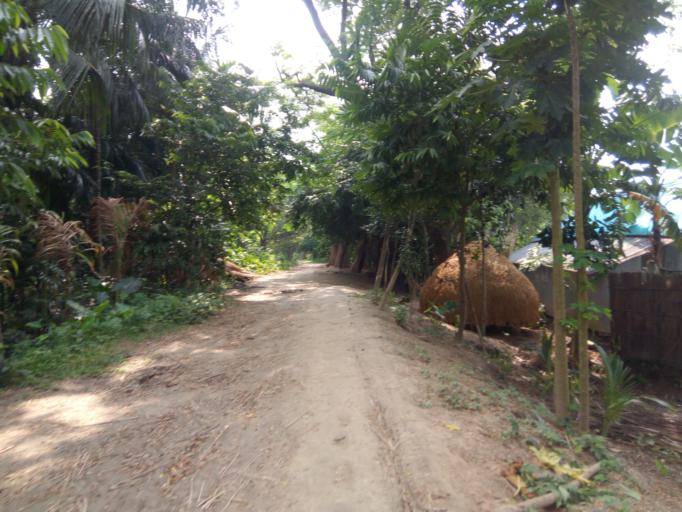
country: BD
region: Khulna
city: Kalia
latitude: 23.0593
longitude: 89.6552
